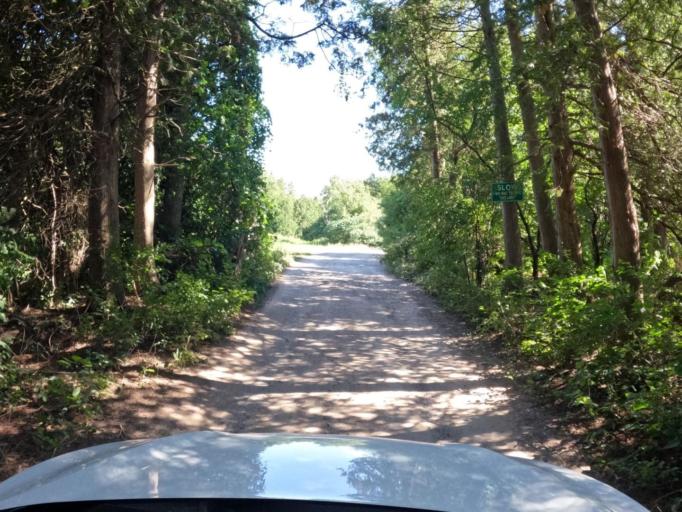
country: CA
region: Ontario
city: Cambridge
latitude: 43.4203
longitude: -80.2527
